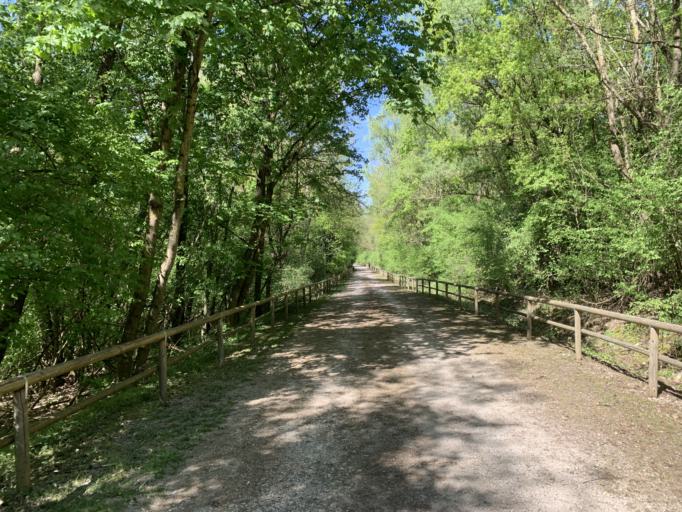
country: DE
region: Bavaria
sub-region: Swabia
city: Gersthofen
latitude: 48.4193
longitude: 10.8925
